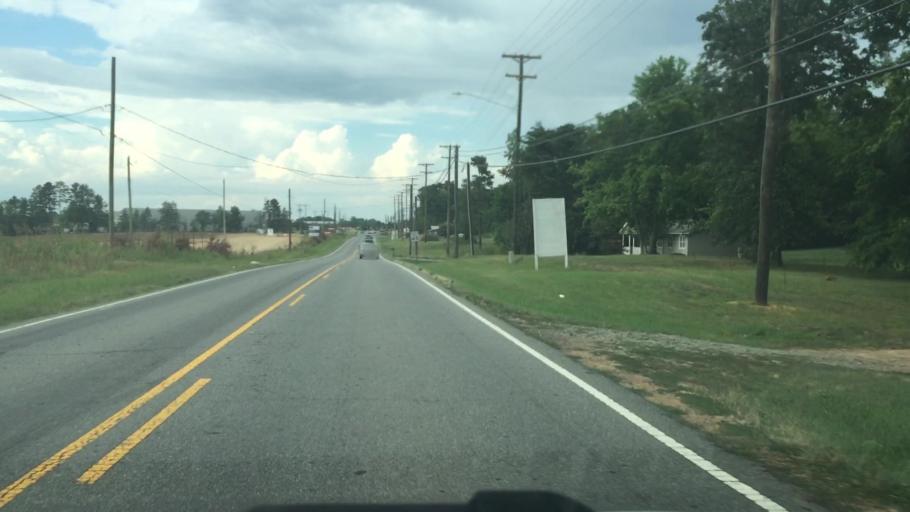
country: US
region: North Carolina
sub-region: Cabarrus County
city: Harrisburg
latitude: 35.3987
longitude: -80.7162
